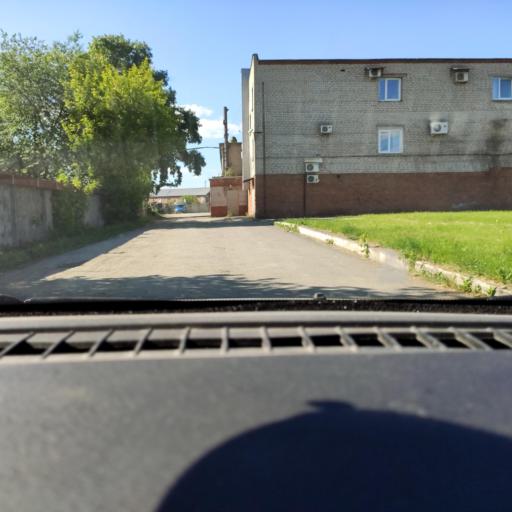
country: RU
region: Perm
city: Froly
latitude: 57.9508
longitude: 56.2554
